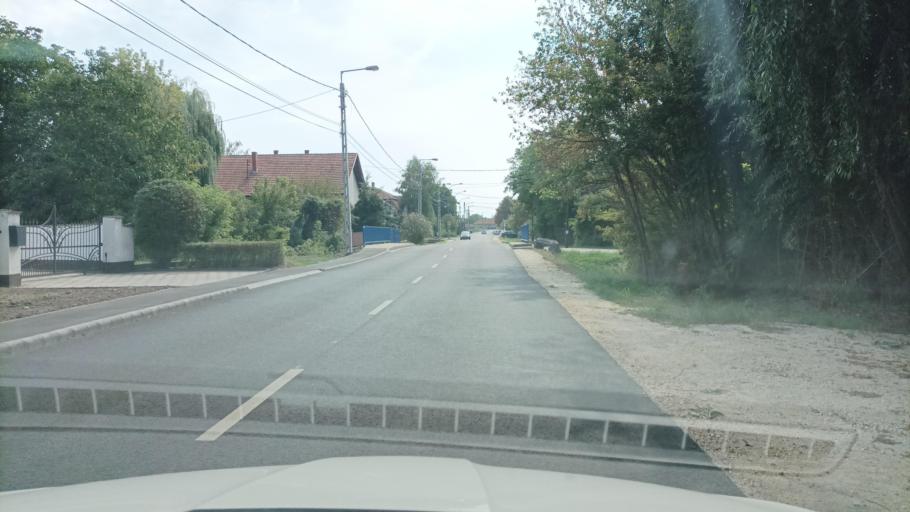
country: HU
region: Pest
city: Tura
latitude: 47.6189
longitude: 19.5978
